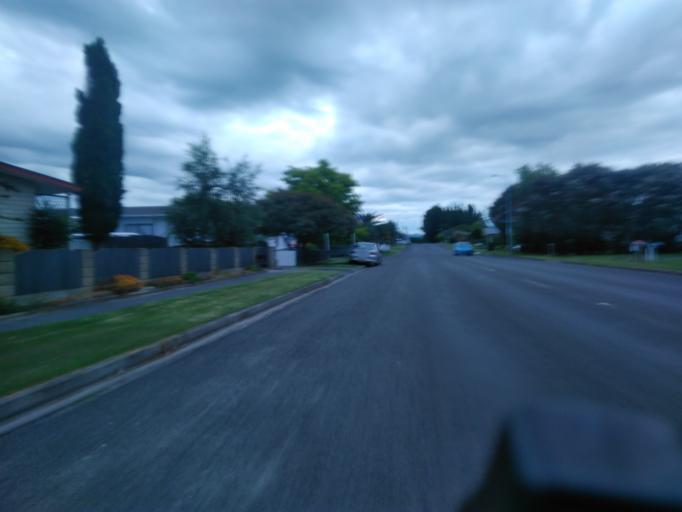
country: NZ
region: Gisborne
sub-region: Gisborne District
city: Gisborne
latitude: -38.6448
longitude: 177.9906
